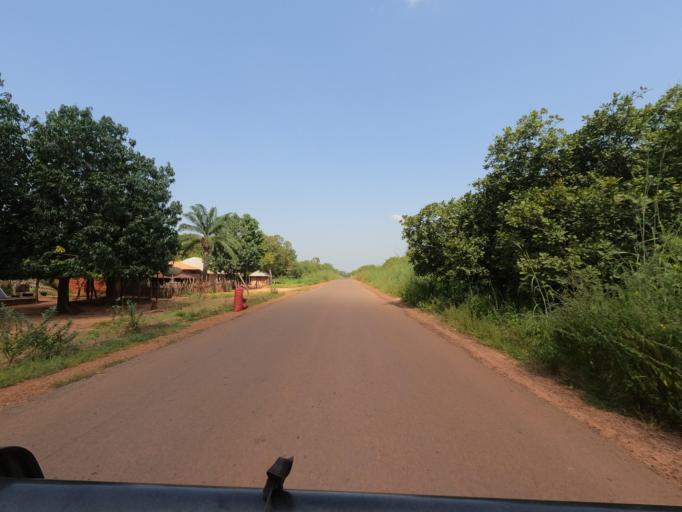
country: SN
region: Ziguinchor
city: Adeane
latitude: 12.3738
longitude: -15.7772
